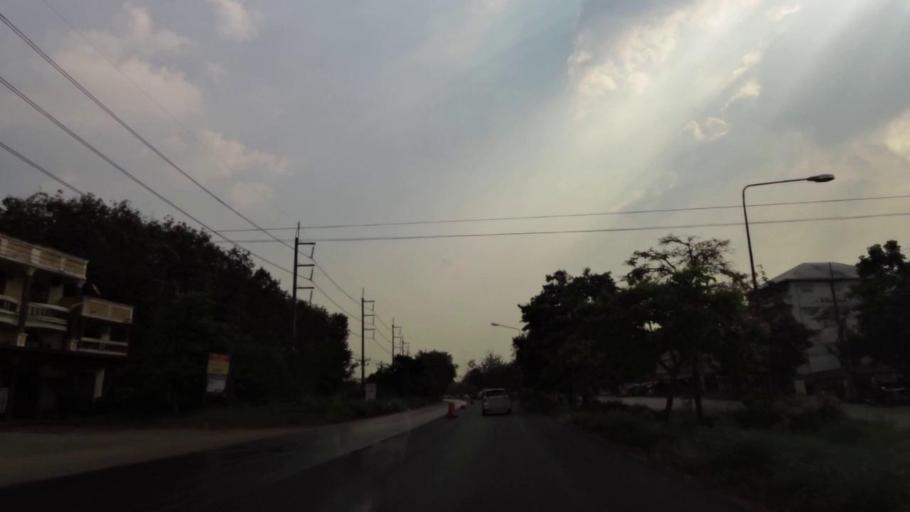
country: TH
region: Rayong
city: Klaeng
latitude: 12.8295
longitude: 101.6280
